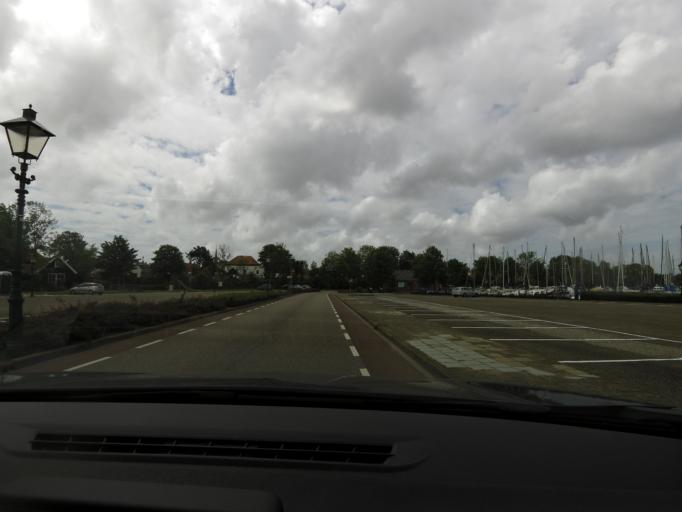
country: NL
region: Zeeland
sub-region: Schouwen-Duiveland
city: Scharendijke
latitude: 51.7275
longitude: 3.9150
